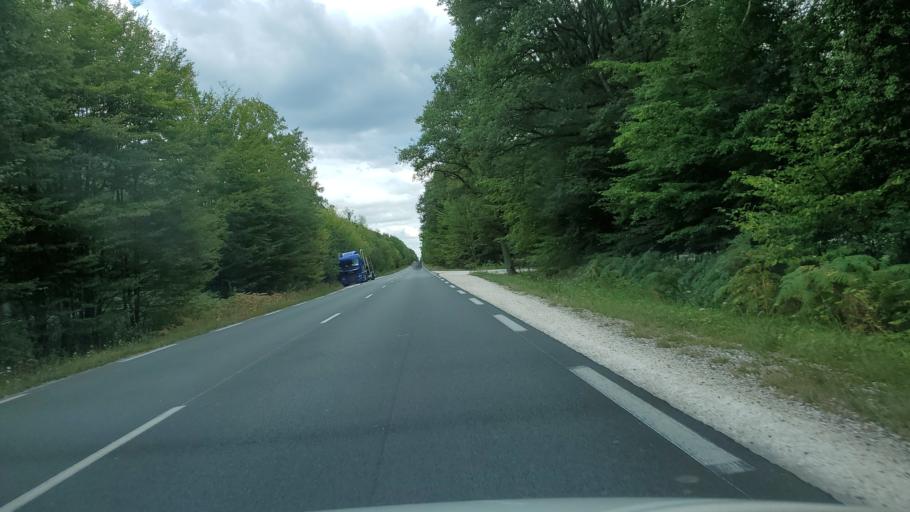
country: FR
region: Ile-de-France
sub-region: Departement de Seine-et-Marne
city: Mortcerf
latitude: 48.7802
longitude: 2.8910
